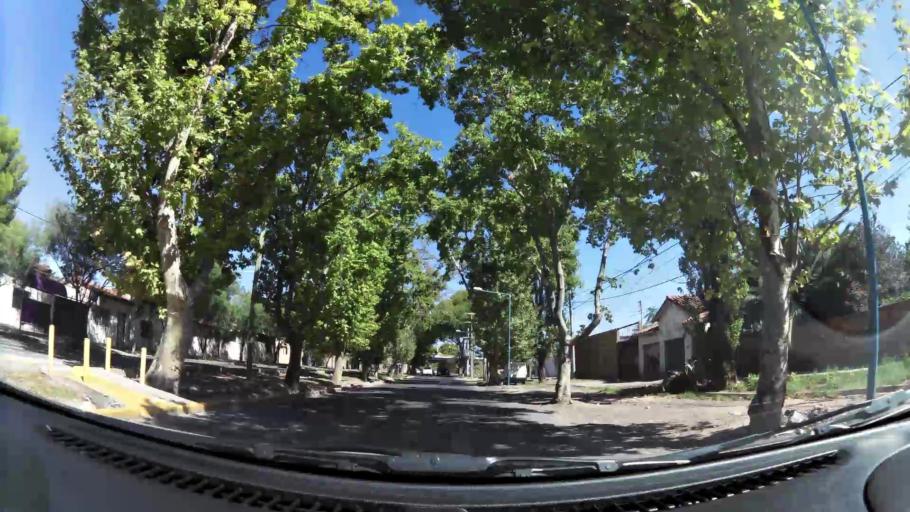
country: AR
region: Mendoza
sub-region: Departamento de Godoy Cruz
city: Godoy Cruz
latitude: -32.9409
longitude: -68.8287
